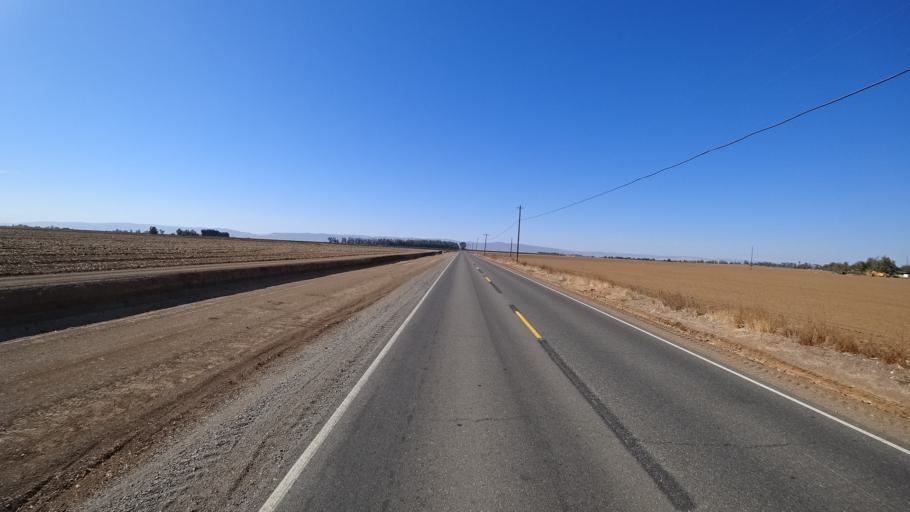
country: US
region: California
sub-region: Yolo County
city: Woodland
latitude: 38.6197
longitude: -121.8506
